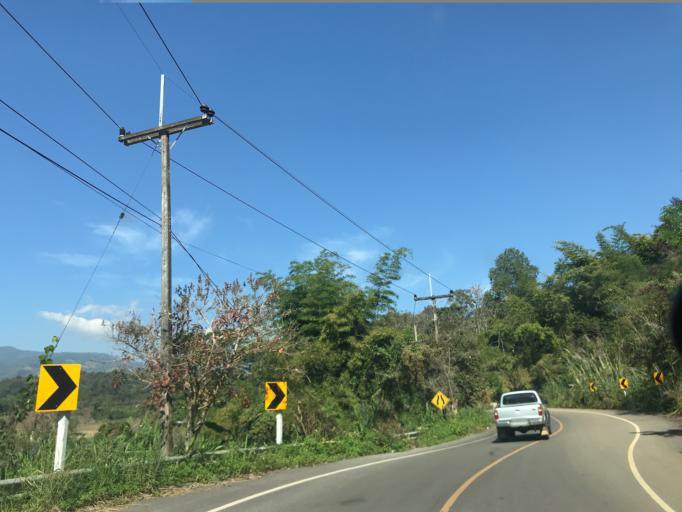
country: TH
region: Chiang Rai
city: Mae Lao
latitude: 19.8083
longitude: 99.6463
